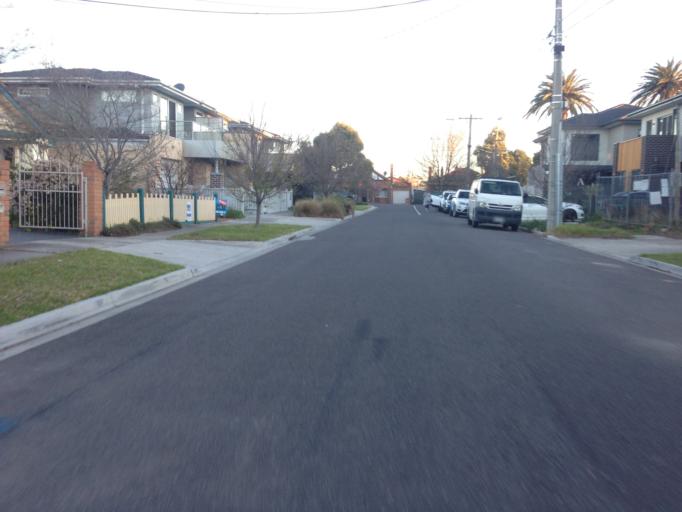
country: AU
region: Victoria
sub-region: Darebin
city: Fairfield
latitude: -37.7749
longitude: 145.0134
